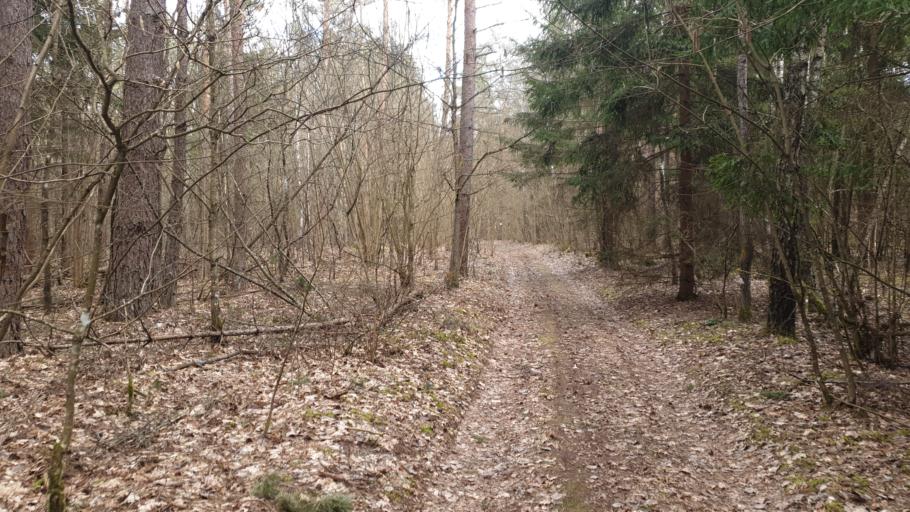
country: LT
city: Grigiskes
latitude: 54.7255
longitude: 25.0339
